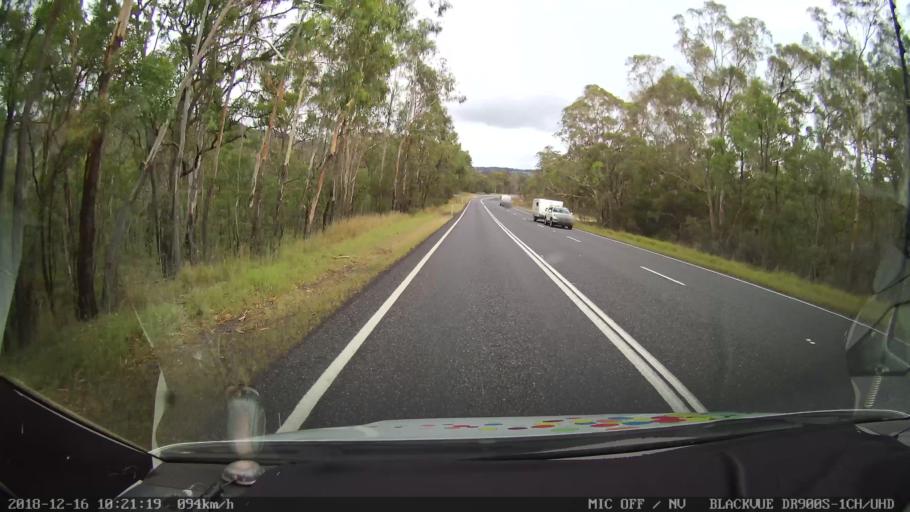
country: AU
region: New South Wales
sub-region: Tenterfield Municipality
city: Carrolls Creek
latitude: -29.2086
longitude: 152.0129
